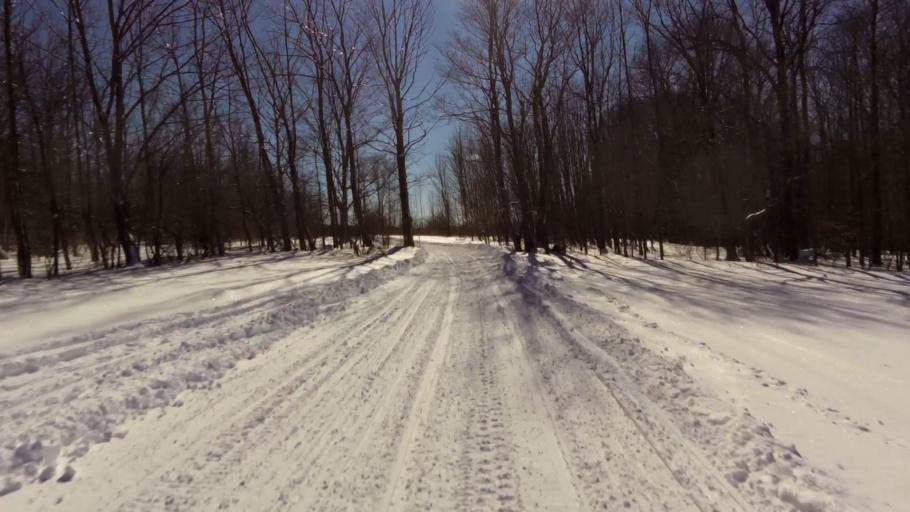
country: US
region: New York
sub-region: Chautauqua County
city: Mayville
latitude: 42.2336
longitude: -79.3939
